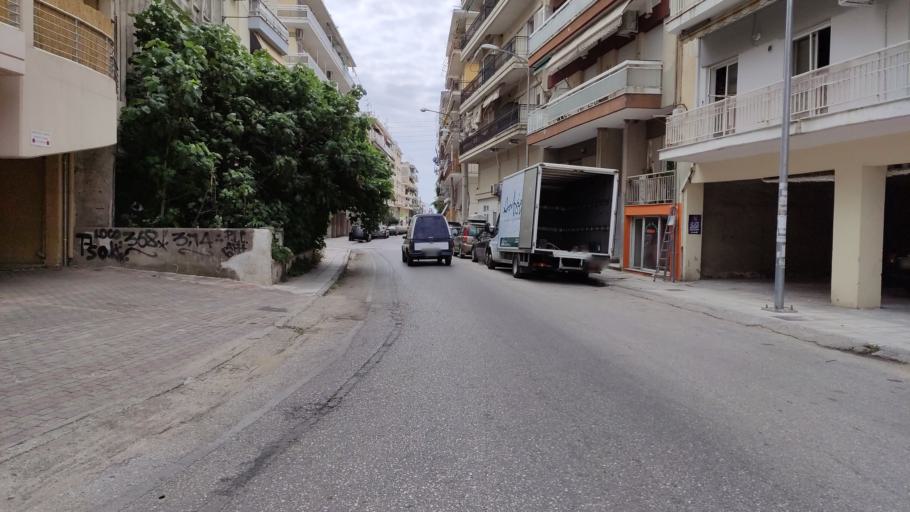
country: GR
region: East Macedonia and Thrace
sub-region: Nomos Rodopis
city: Komotini
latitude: 41.1193
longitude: 25.3958
